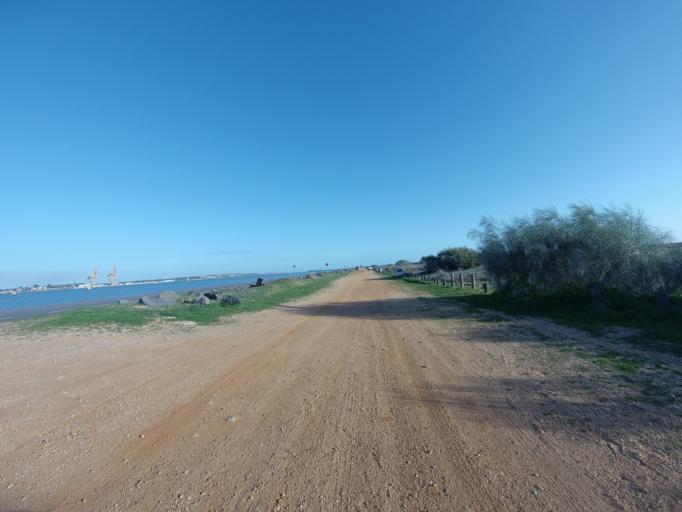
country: ES
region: Andalusia
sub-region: Provincia de Huelva
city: Punta Umbria
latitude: 37.1488
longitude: -6.8943
